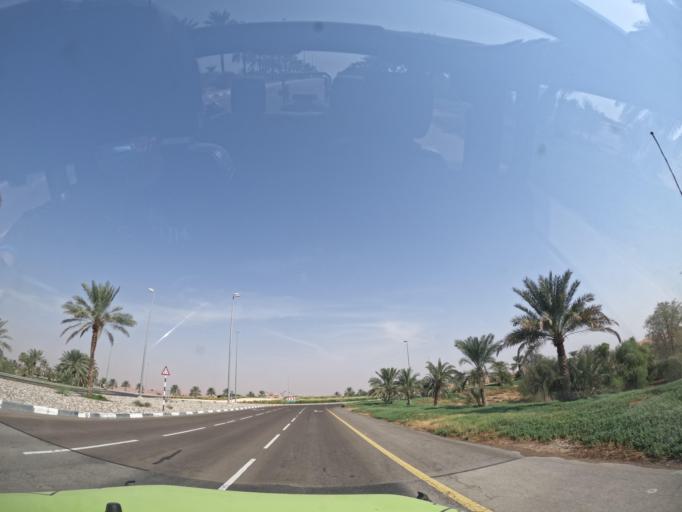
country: AE
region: Abu Dhabi
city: Al Ain
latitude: 24.2616
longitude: 55.6699
